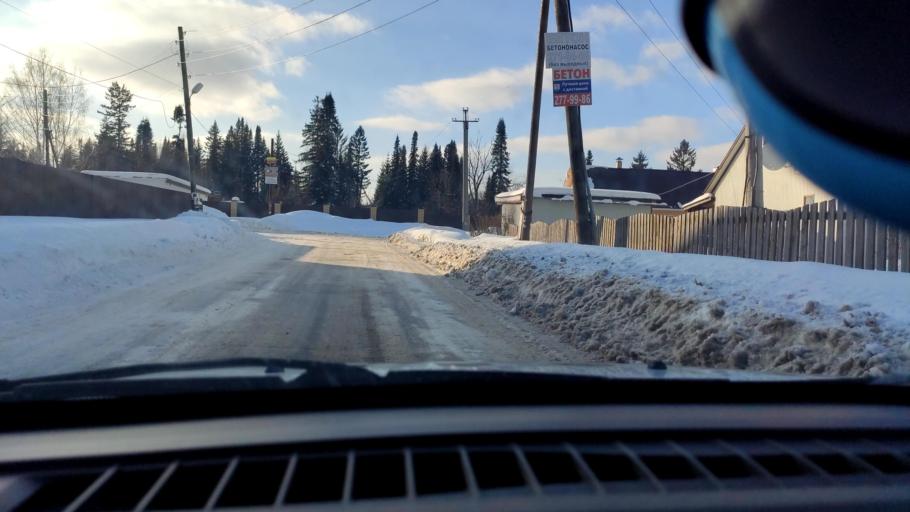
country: RU
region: Perm
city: Kultayevo
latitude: 57.9377
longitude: 55.8593
